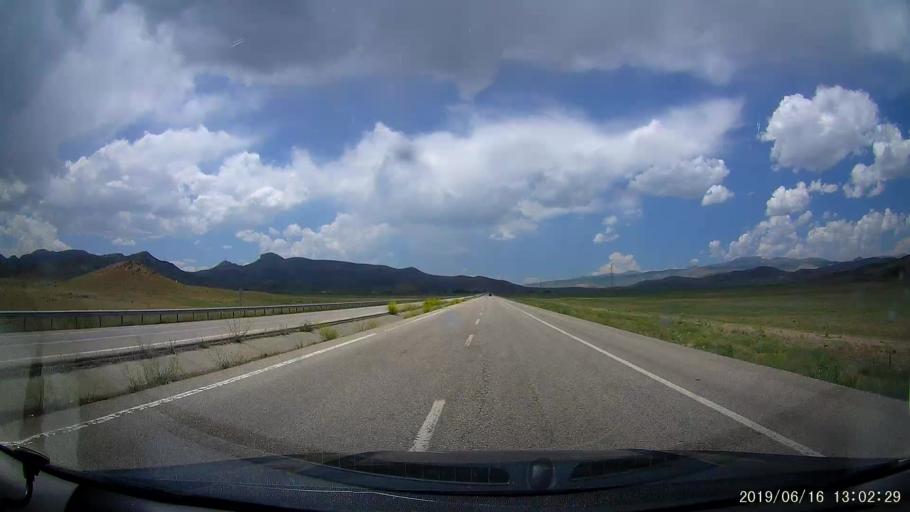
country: TR
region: Agri
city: Sulucem
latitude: 39.5749
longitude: 43.8152
